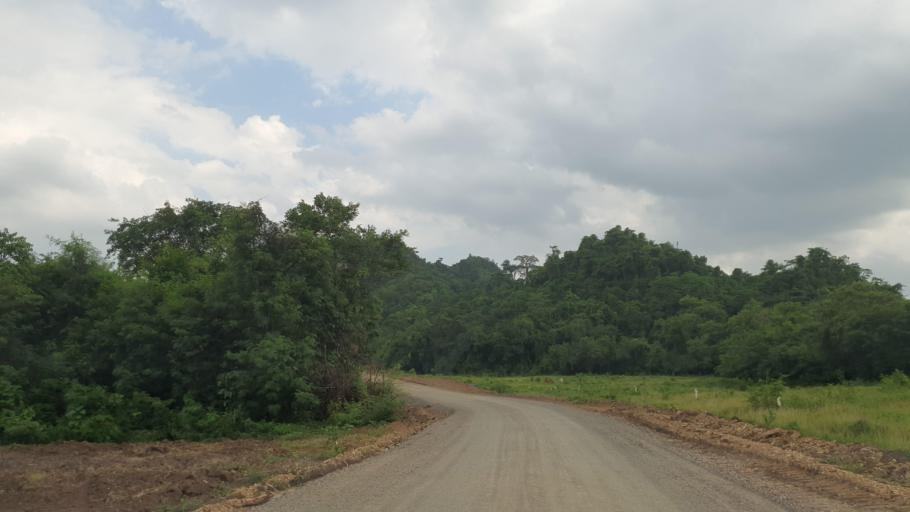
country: TH
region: Sukhothai
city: Thung Saliam
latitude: 17.2634
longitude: 99.5383
